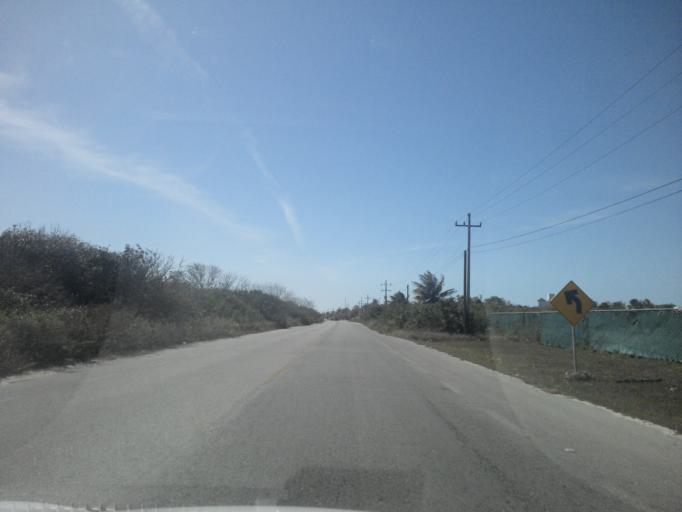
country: MX
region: Yucatan
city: Telchac Puerto
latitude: 21.3308
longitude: -89.3765
